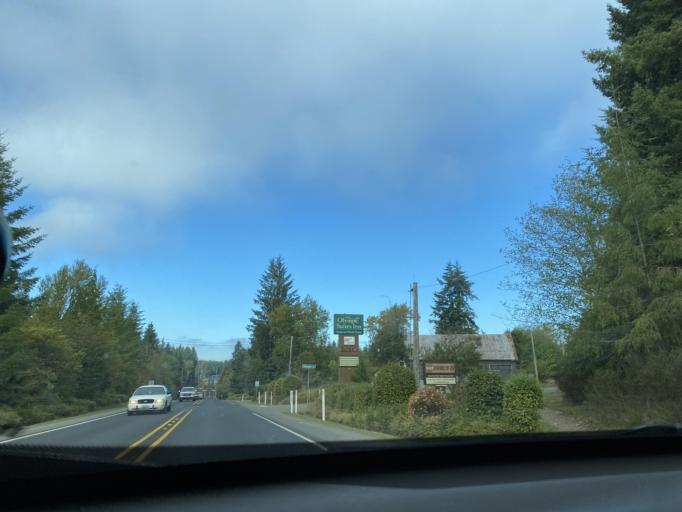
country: US
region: Washington
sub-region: Clallam County
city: Forks
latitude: 47.9576
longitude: -124.3887
